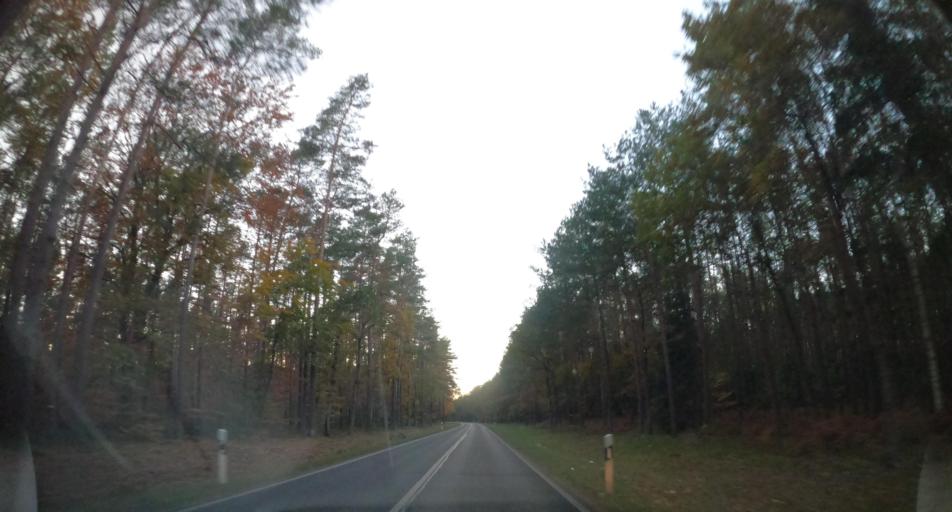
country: DE
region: Mecklenburg-Vorpommern
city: Ueckermunde
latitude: 53.7669
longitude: 13.9519
